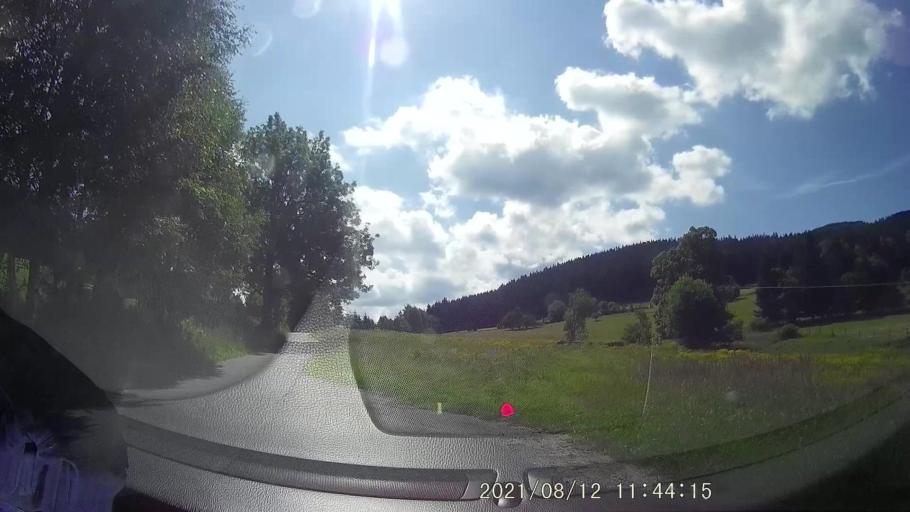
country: PL
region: Lower Silesian Voivodeship
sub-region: Powiat klodzki
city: Stronie Slaskie
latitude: 50.2571
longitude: 16.8360
